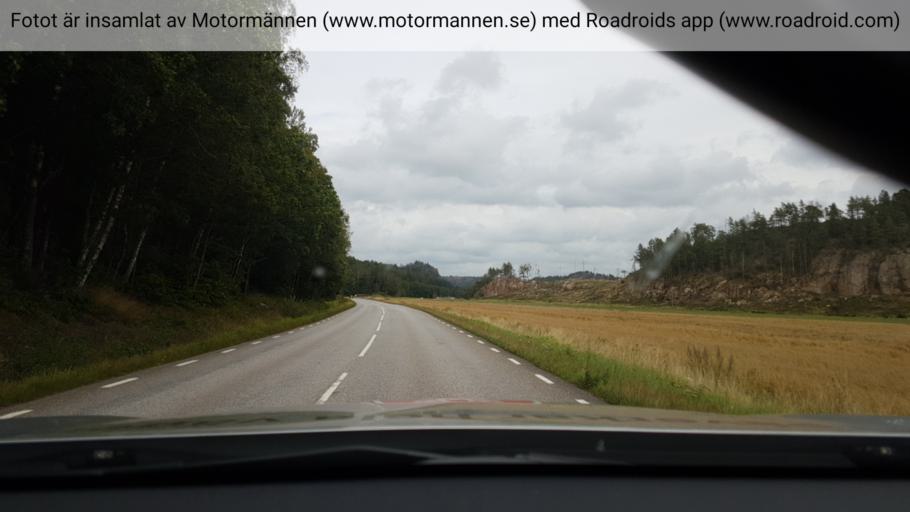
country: SE
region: Vaestra Goetaland
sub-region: Lysekils Kommun
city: Brastad
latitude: 58.5513
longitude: 11.4399
